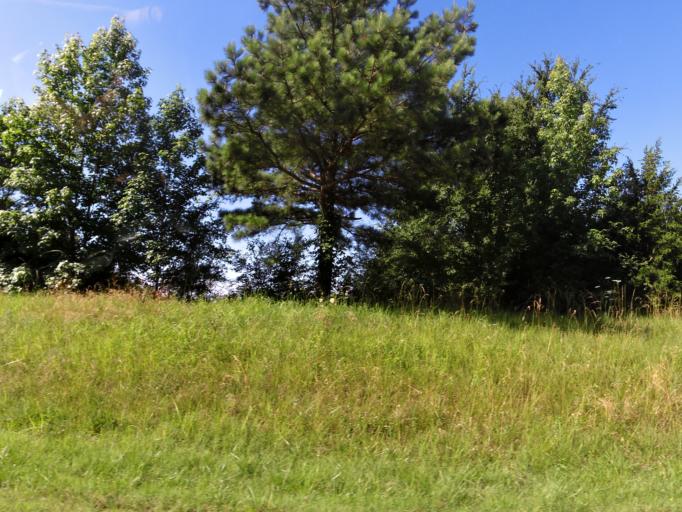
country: US
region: Arkansas
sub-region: Clay County
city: Piggott
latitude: 36.4328
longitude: -90.2569
